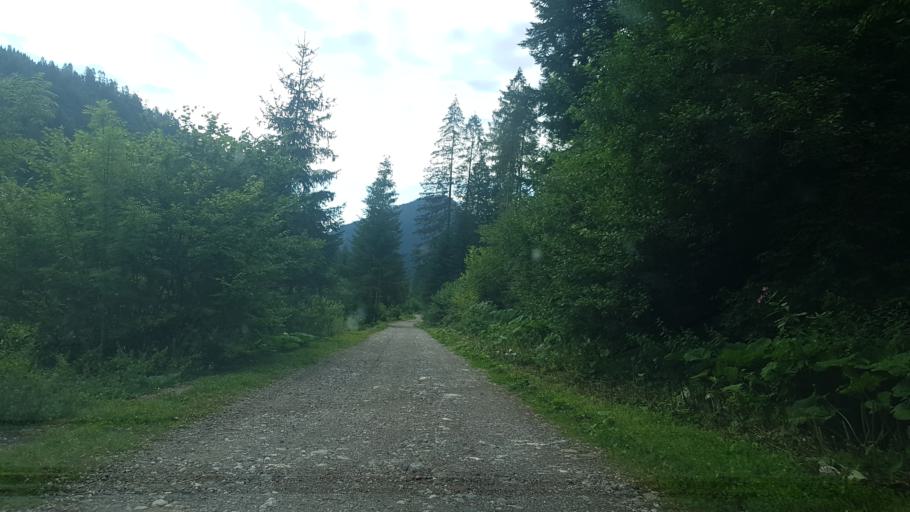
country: IT
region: Friuli Venezia Giulia
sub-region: Provincia di Udine
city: Forni Avoltri
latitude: 46.5810
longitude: 12.7830
